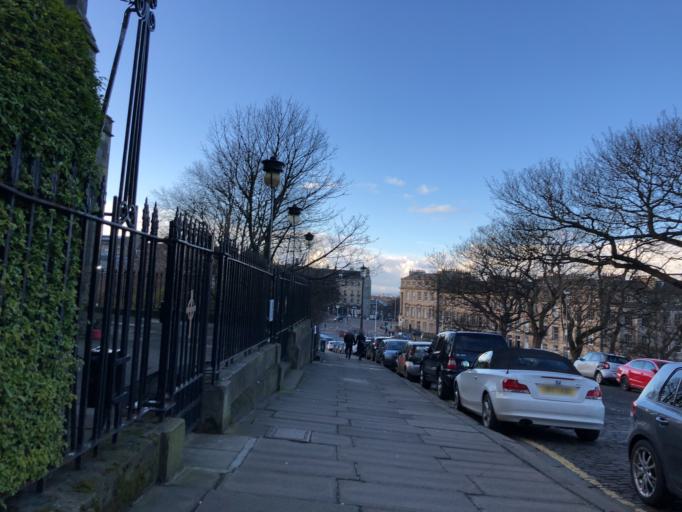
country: GB
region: Scotland
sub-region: Edinburgh
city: Edinburgh
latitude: 55.9571
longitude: -3.1817
